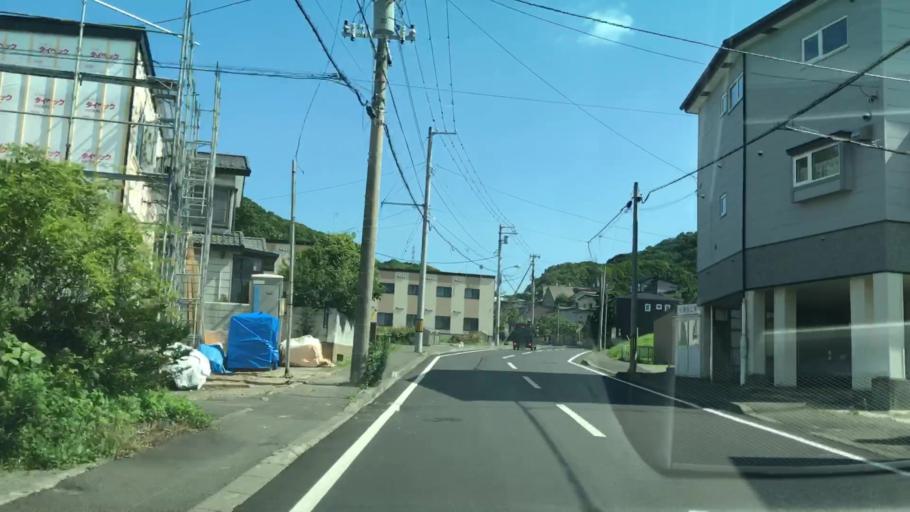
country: JP
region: Hokkaido
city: Muroran
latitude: 42.3098
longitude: 140.9978
